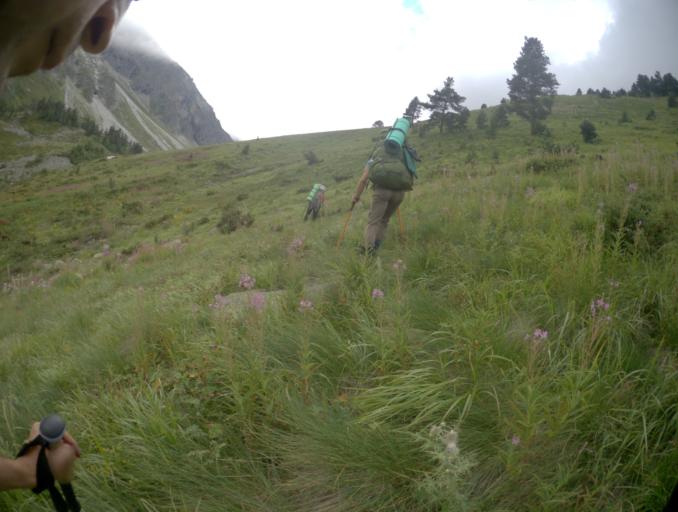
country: RU
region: Karachayevo-Cherkesiya
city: Uchkulan
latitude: 43.3386
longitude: 42.1307
